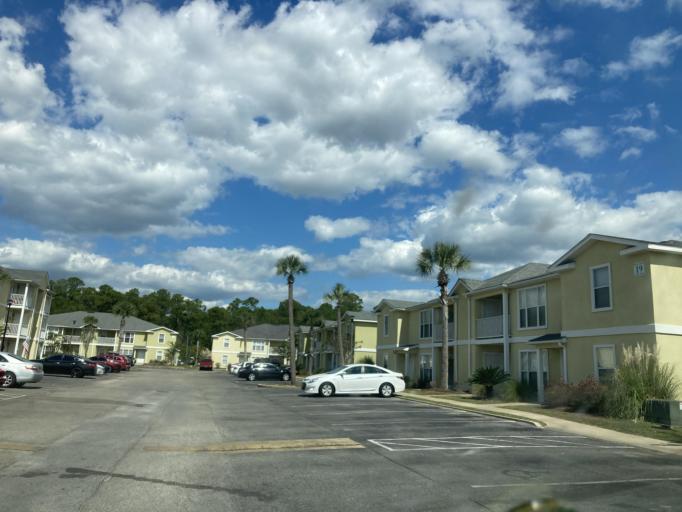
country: US
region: Mississippi
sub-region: Jackson County
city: Saint Martin
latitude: 30.4451
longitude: -88.8523
